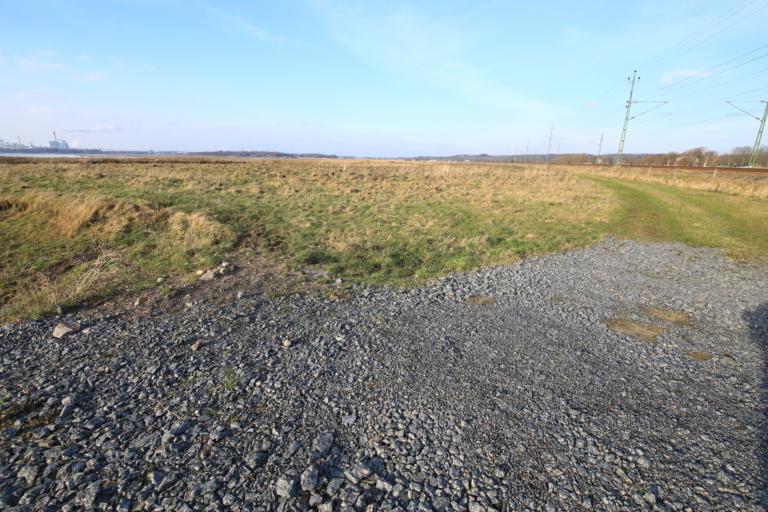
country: SE
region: Halland
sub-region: Varbergs Kommun
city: Veddige
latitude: 57.2168
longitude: 12.2197
